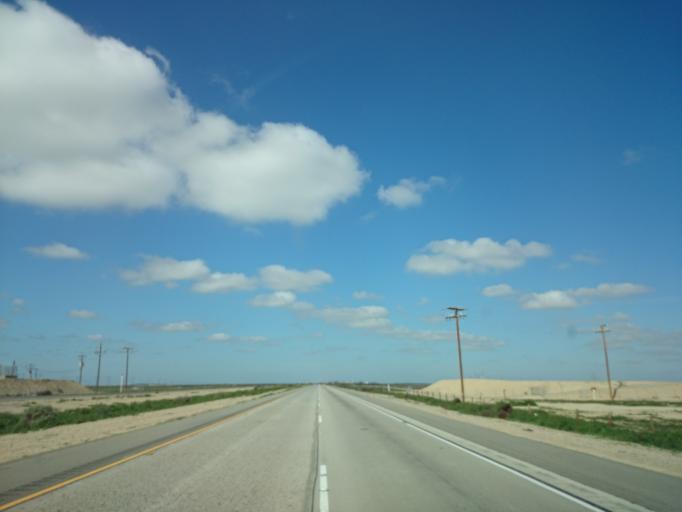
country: US
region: California
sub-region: Kern County
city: Rosedale
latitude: 35.3322
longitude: -119.3036
